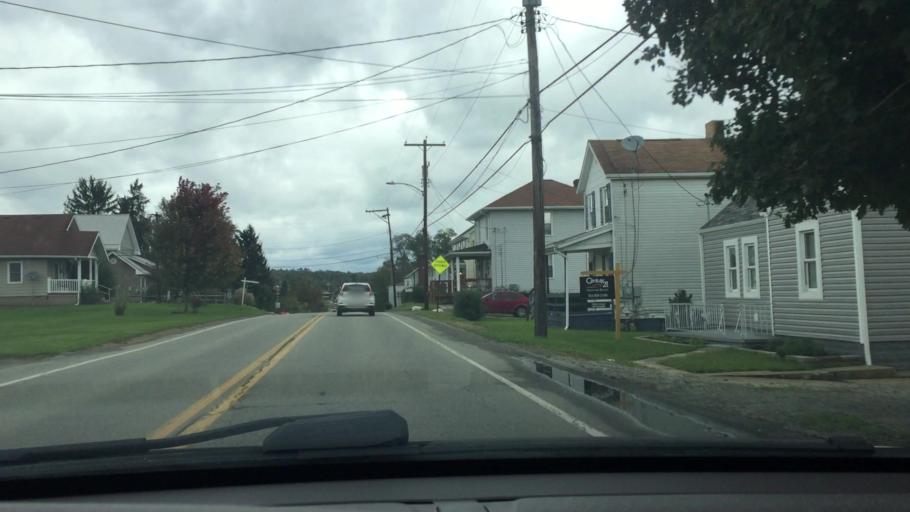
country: US
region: Pennsylvania
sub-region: Westmoreland County
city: Lynnwood-Pricedale
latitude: 40.1309
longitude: -79.8444
